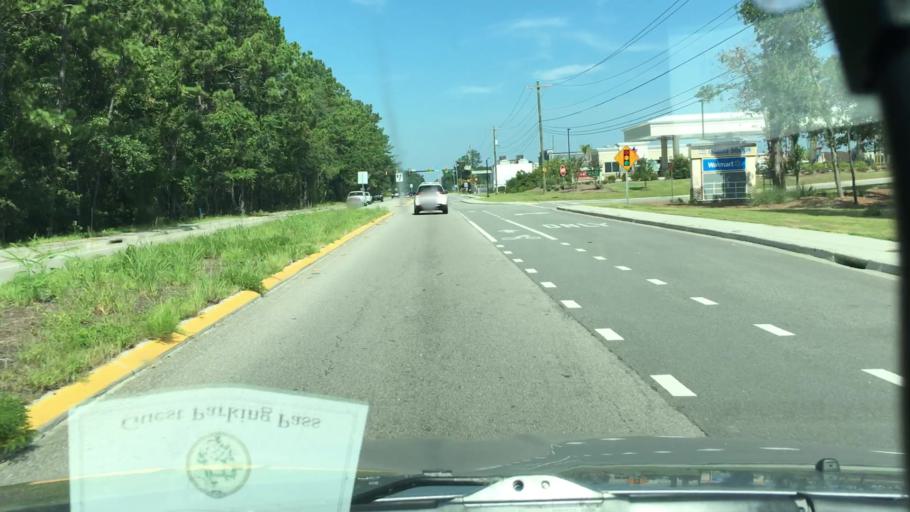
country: US
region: South Carolina
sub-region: Beaufort County
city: Beaufort
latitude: 32.4061
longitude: -80.6348
